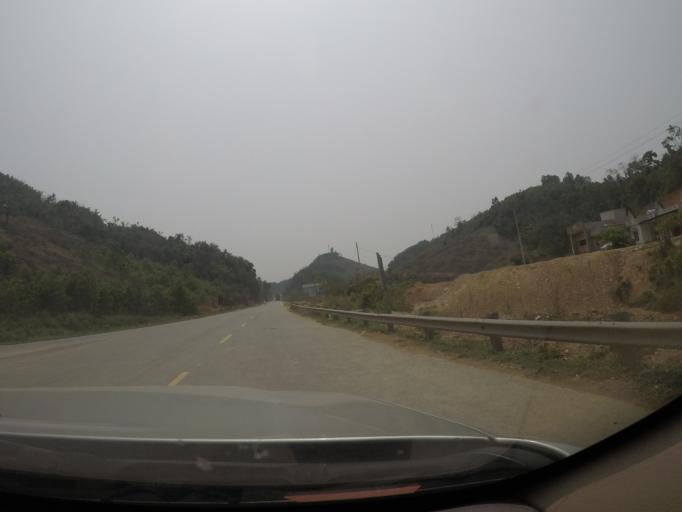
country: VN
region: Thanh Hoa
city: Thi Tran Yen Cat
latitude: 19.6764
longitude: 105.4553
